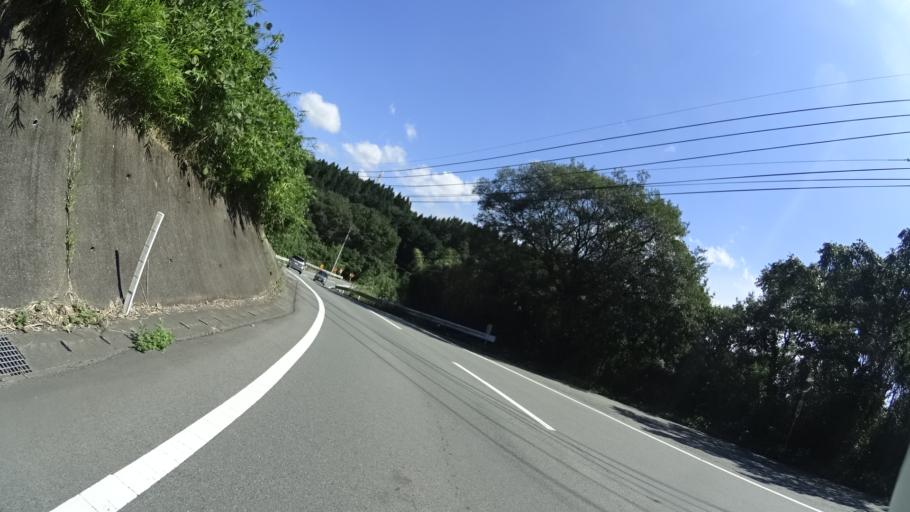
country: JP
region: Kumamoto
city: Aso
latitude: 32.8924
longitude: 130.9916
